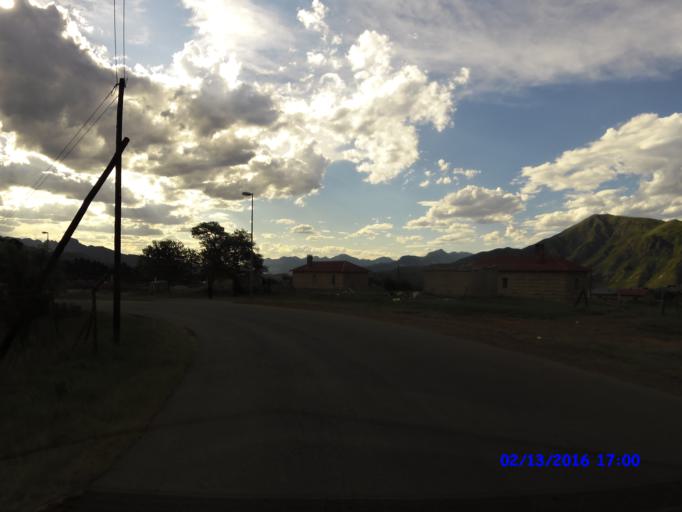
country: LS
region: Qacha's Nek
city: Qacha's Nek
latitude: -30.1139
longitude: 28.6894
